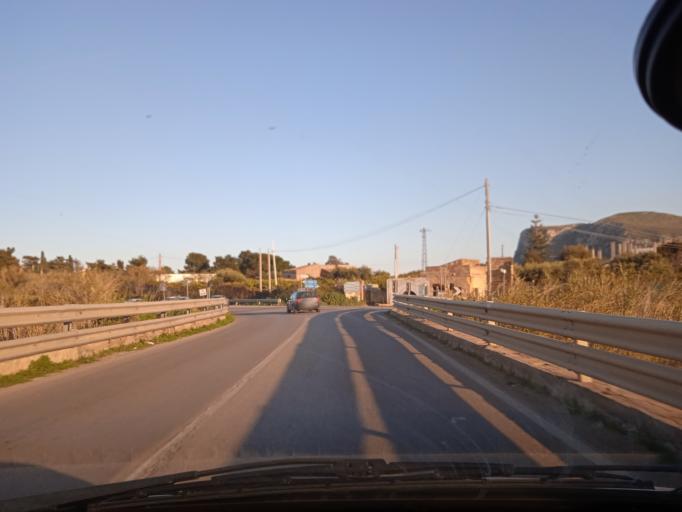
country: IT
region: Sicily
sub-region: Palermo
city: Ficarazzi
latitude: 38.0916
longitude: 13.4778
